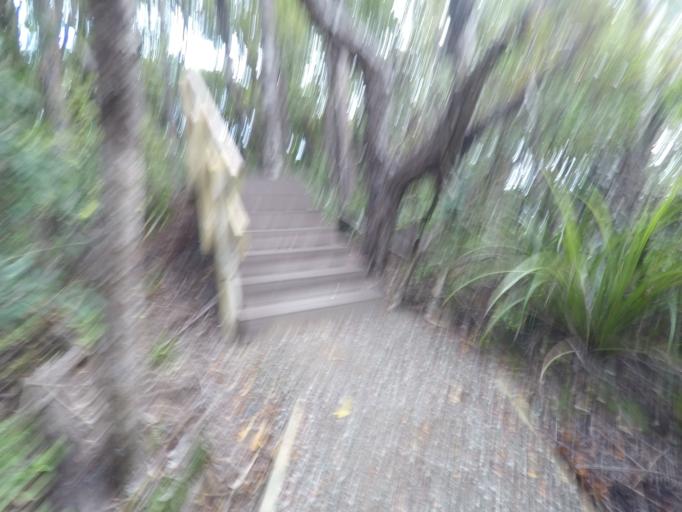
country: NZ
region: Auckland
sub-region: Auckland
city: Titirangi
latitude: -37.0278
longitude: 174.5288
